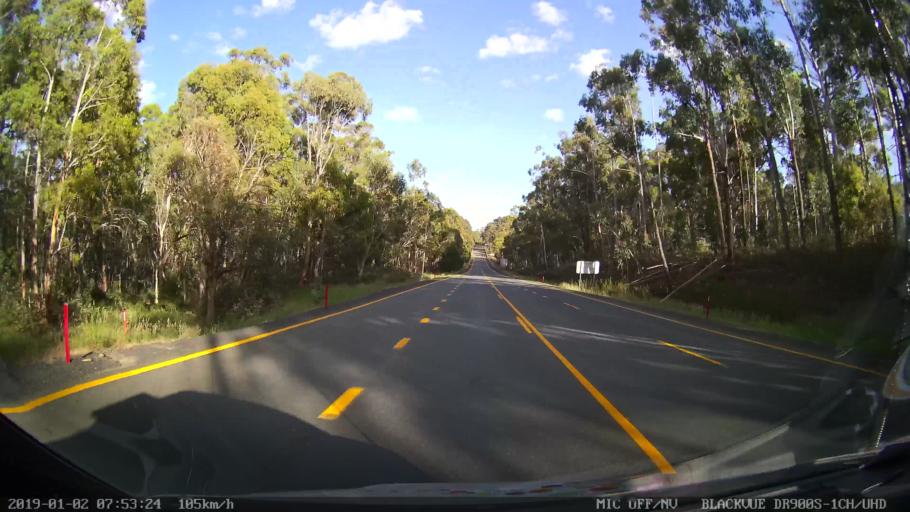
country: AU
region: New South Wales
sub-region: Tumut Shire
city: Tumut
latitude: -35.7058
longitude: 148.5069
